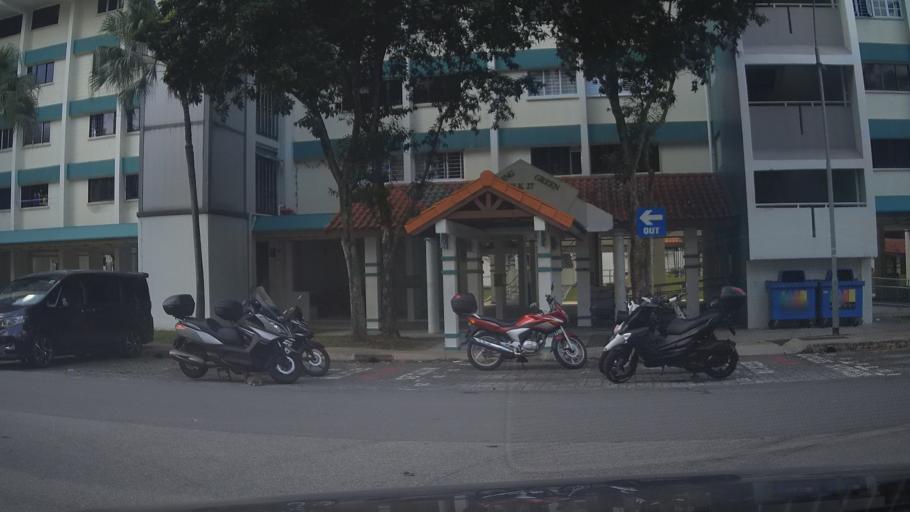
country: MY
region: Johor
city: Johor Bahru
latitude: 1.4427
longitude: 103.7739
